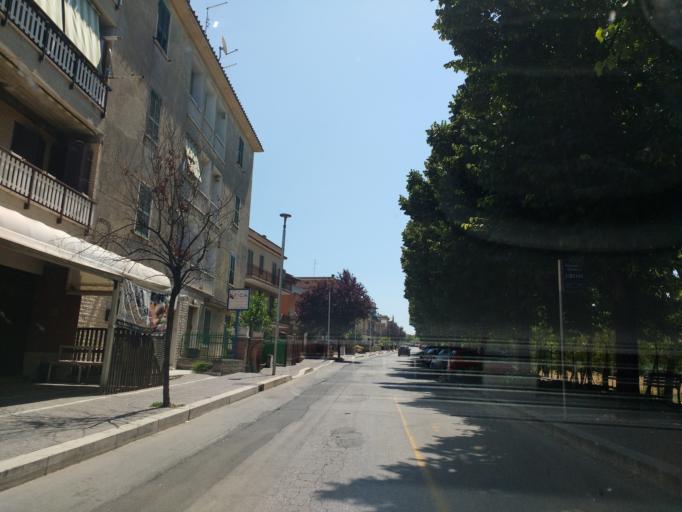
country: IT
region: Latium
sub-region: Citta metropolitana di Roma Capitale
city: Villa Adriana
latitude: 41.9503
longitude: 12.7708
